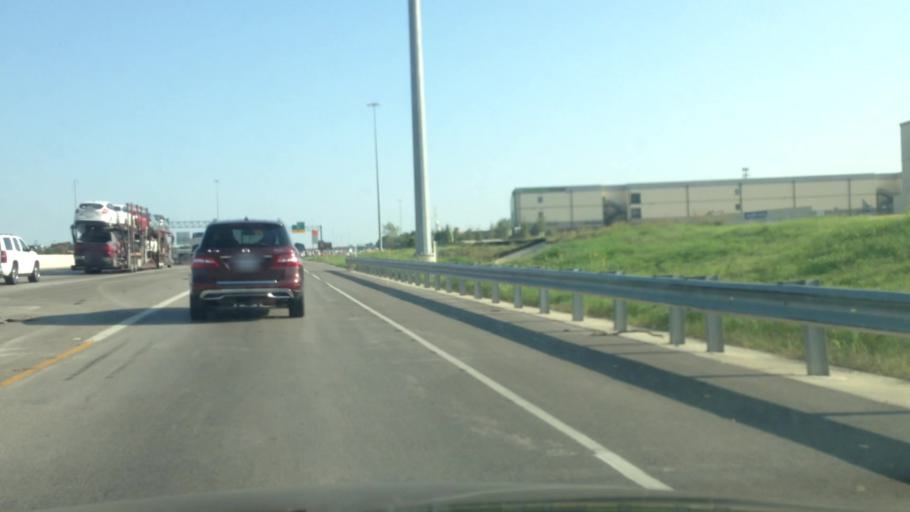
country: US
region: Texas
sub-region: Tarrant County
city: Blue Mound
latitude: 32.8562
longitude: -97.3138
